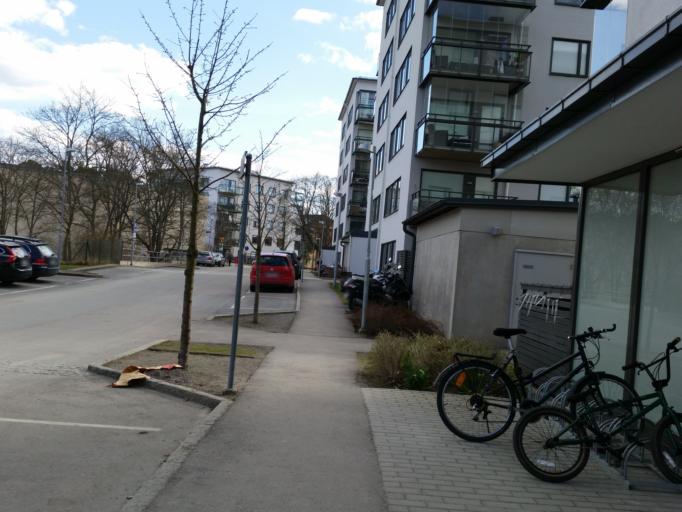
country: SE
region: Stockholm
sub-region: Sundbybergs Kommun
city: Sundbyberg
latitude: 59.3699
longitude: 17.9635
